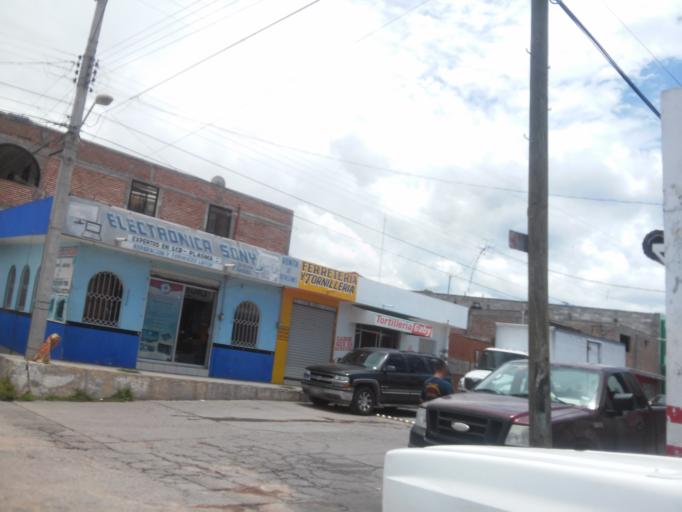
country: MX
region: Durango
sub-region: Santiago Papasquiaro
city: Santiago Papasquiaro
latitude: 25.0487
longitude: -105.4217
